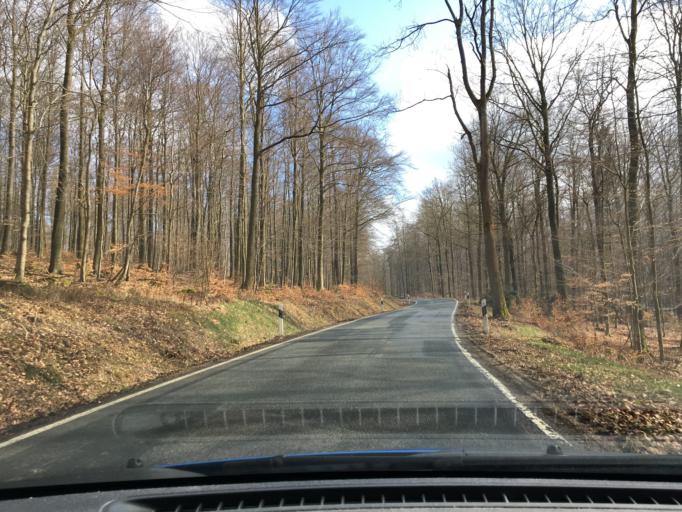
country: DE
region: Lower Saxony
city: Buhren
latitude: 51.5014
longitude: 9.6407
